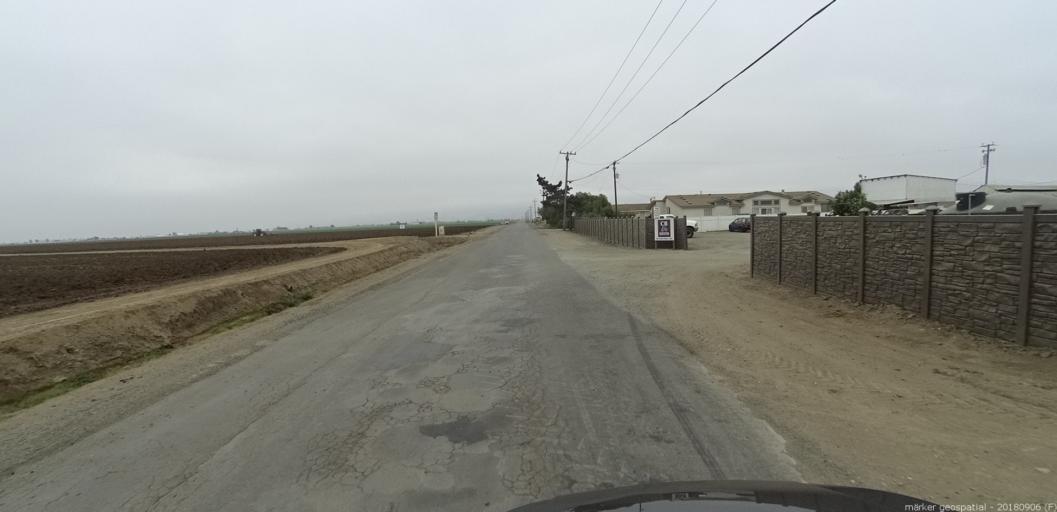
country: US
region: California
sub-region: Monterey County
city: Salinas
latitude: 36.6343
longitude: -121.5803
